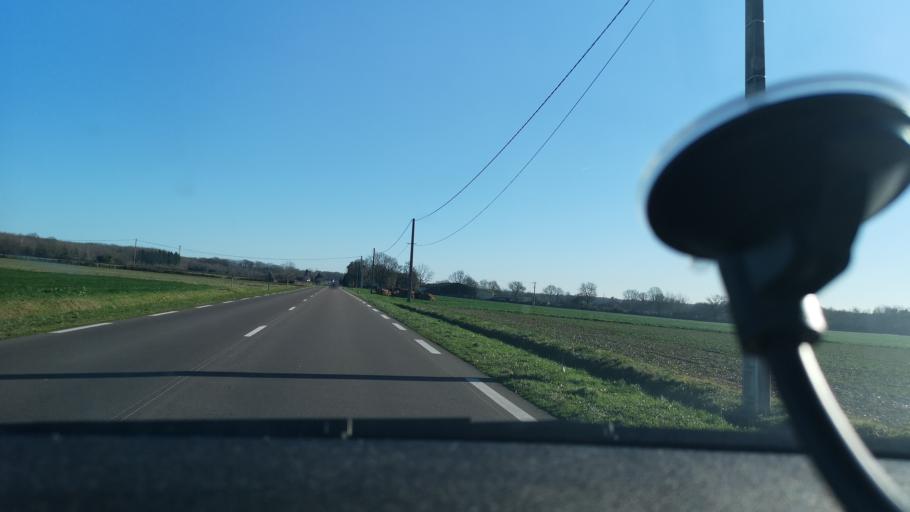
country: FR
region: Bourgogne
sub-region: Departement de Saone-et-Loire
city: Ouroux-sur-Saone
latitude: 46.7737
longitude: 4.9649
